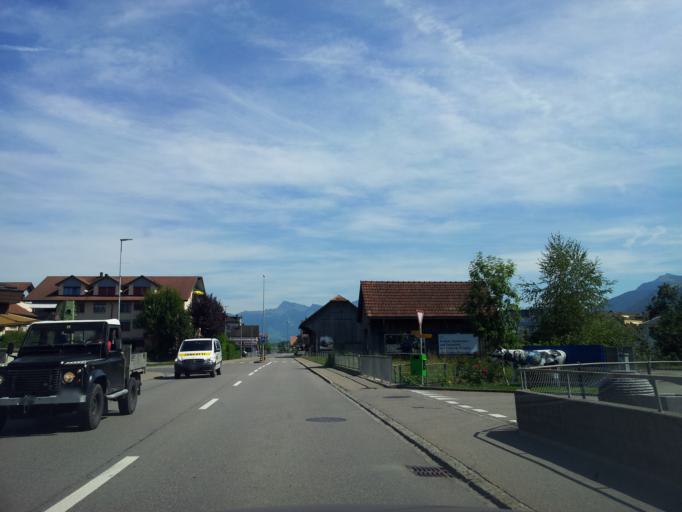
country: CH
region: Schwyz
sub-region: Bezirk March
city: Lachen
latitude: 47.1914
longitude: 8.8923
